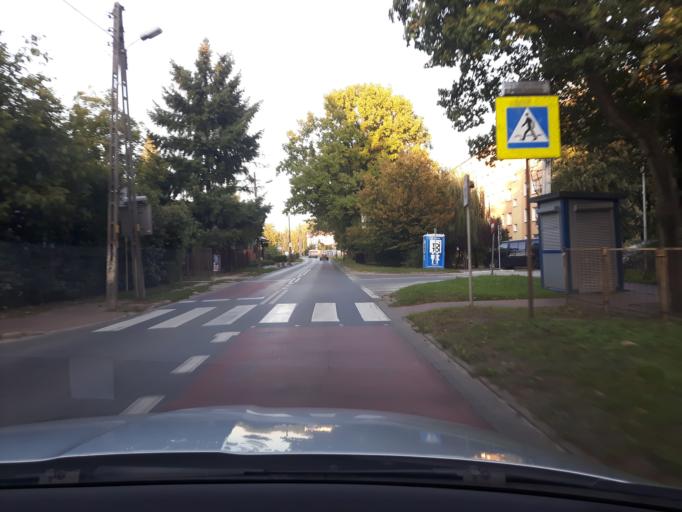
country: PL
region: Masovian Voivodeship
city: Zielonka
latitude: 52.3161
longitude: 21.1611
